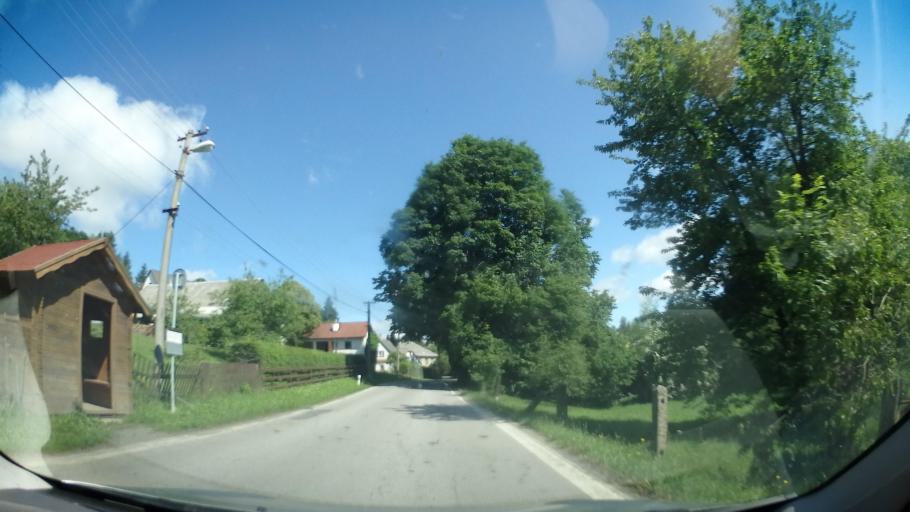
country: CZ
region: Vysocina
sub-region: Okres Zd'ar nad Sazavou
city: Nove Mesto na Morave
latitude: 49.6416
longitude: 16.1196
